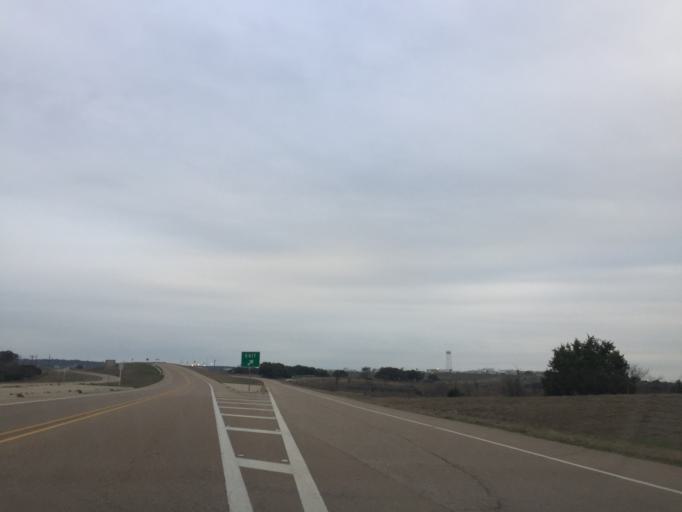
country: US
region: Texas
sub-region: Coryell County
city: Gatesville
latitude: 31.4869
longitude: -97.7379
